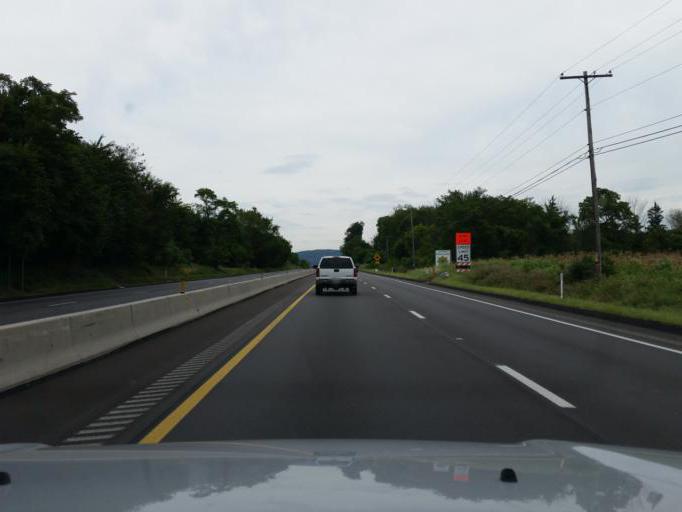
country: US
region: Pennsylvania
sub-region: Westmoreland County
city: Lawson Heights
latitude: 40.2834
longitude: -79.4212
